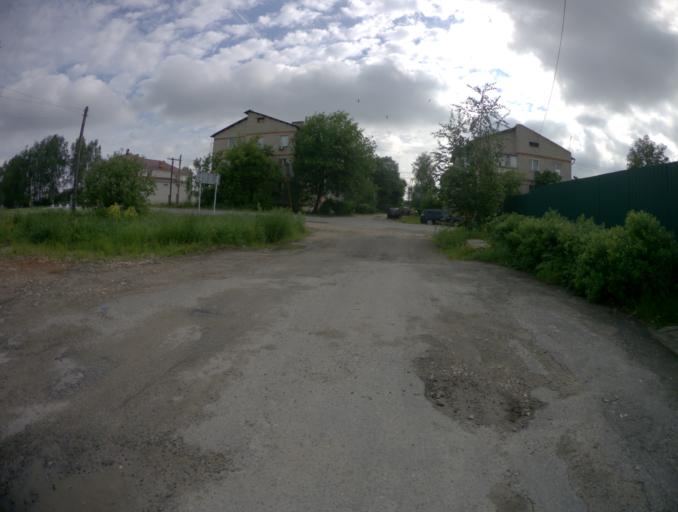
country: RU
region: Vladimir
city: Lakinsk
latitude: 56.0255
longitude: 39.9875
